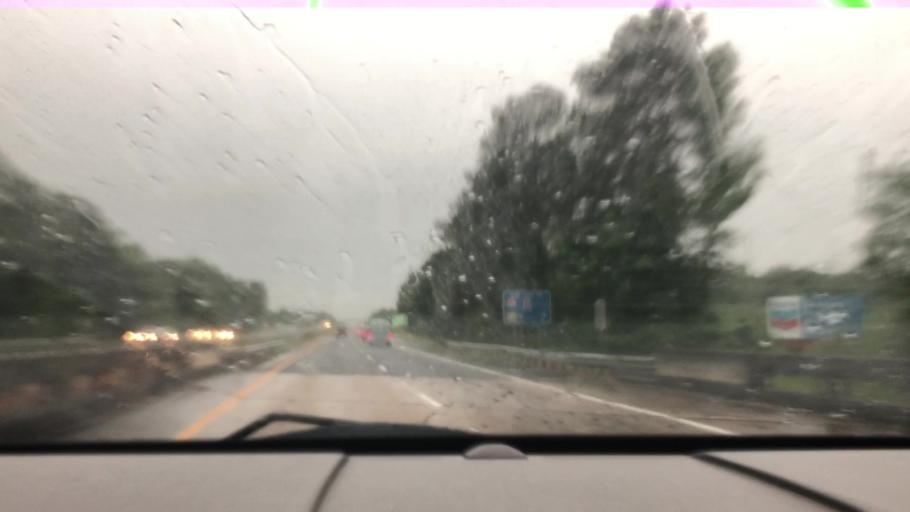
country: US
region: Alabama
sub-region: Butler County
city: Georgiana
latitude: 31.6572
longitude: -86.7694
